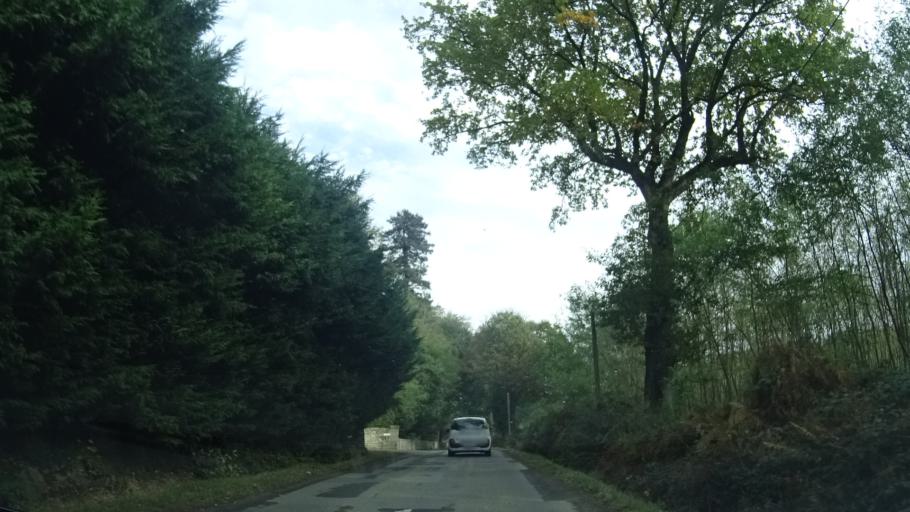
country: FR
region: Brittany
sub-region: Departement d'Ille-et-Vilaine
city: Bonnemain
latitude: 48.4578
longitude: -1.7875
